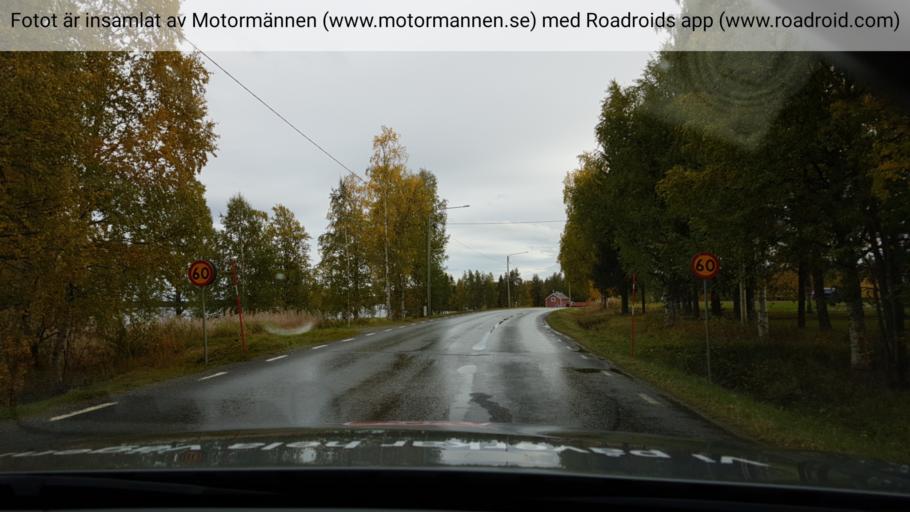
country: SE
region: Vaesterbotten
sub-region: Vilhelmina Kommun
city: Sjoberg
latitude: 64.6466
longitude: 16.3473
